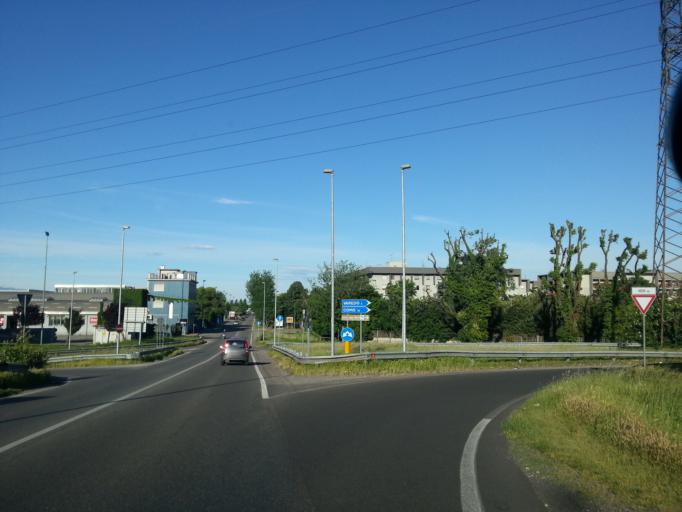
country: IT
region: Lombardy
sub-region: Citta metropolitana di Milano
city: Paderno Dugnano
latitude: 45.5703
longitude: 9.1775
